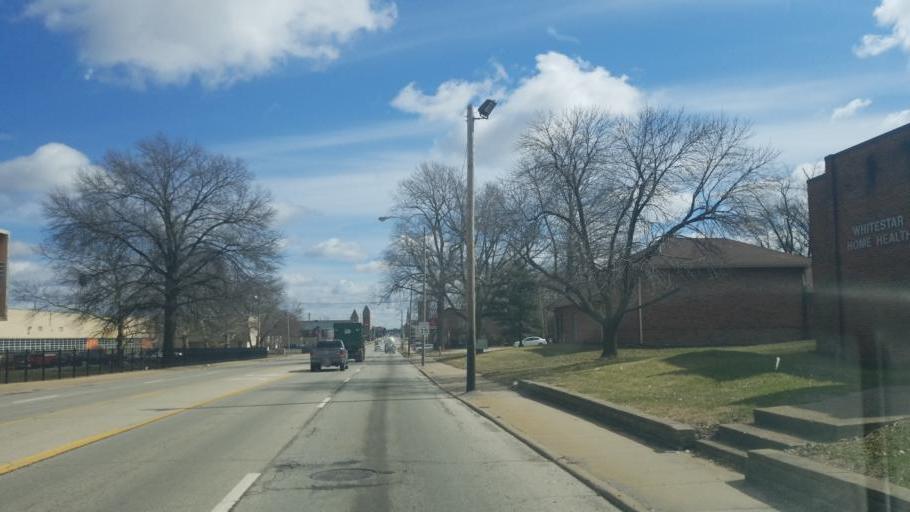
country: US
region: Illinois
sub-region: Macon County
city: Decatur
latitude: 39.8455
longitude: -88.9631
